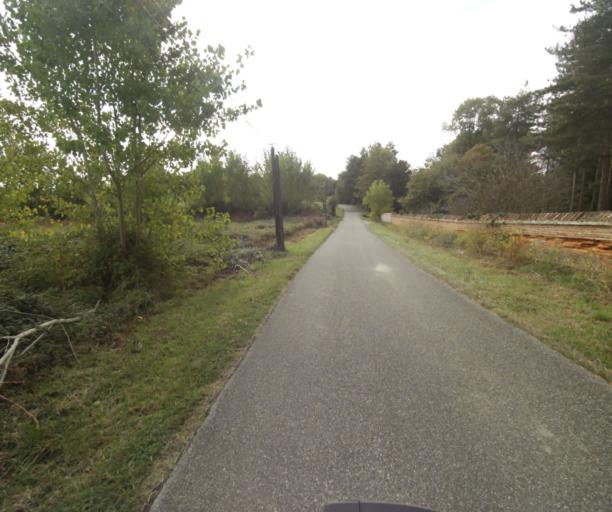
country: FR
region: Midi-Pyrenees
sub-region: Departement du Tarn-et-Garonne
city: Finhan
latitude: 43.9262
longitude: 1.2176
